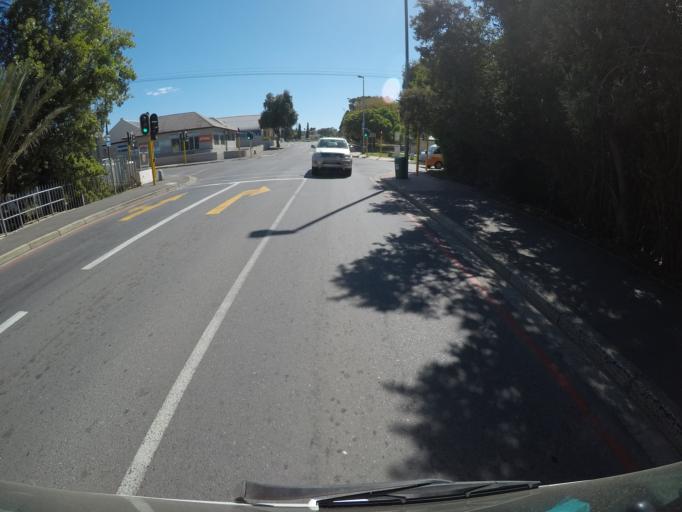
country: ZA
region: Western Cape
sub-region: City of Cape Town
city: Kraaifontein
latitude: -33.8313
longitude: 18.6457
